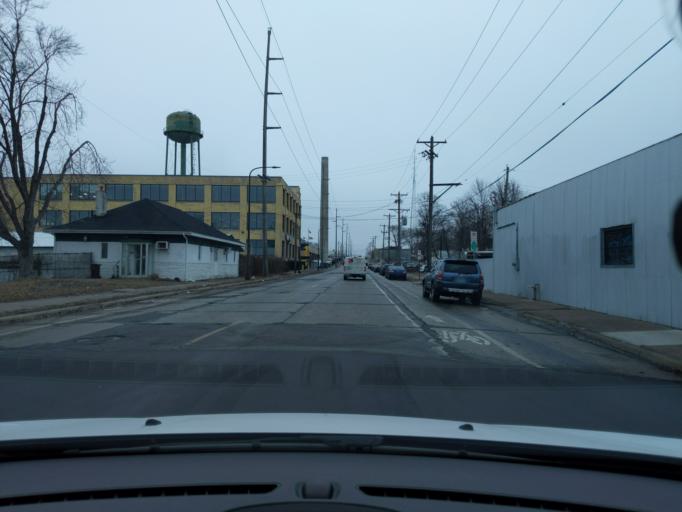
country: US
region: Minnesota
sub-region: Ramsey County
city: Falcon Heights
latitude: 44.9629
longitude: -93.1823
